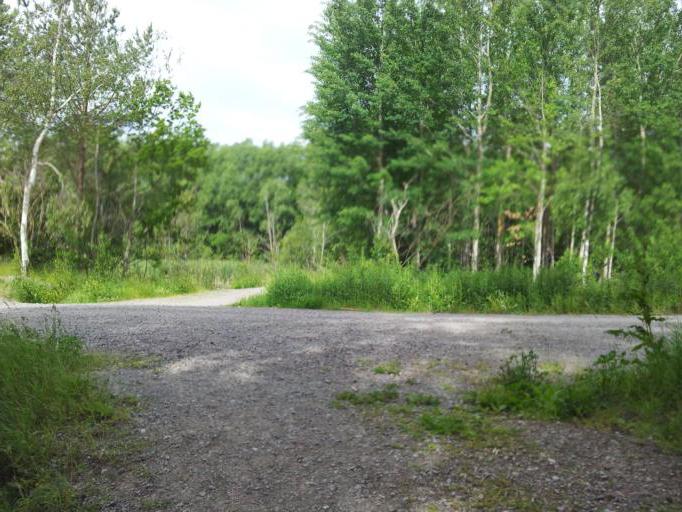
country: SE
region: Uppsala
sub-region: Uppsala Kommun
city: Gamla Uppsala
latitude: 59.8890
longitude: 17.6608
